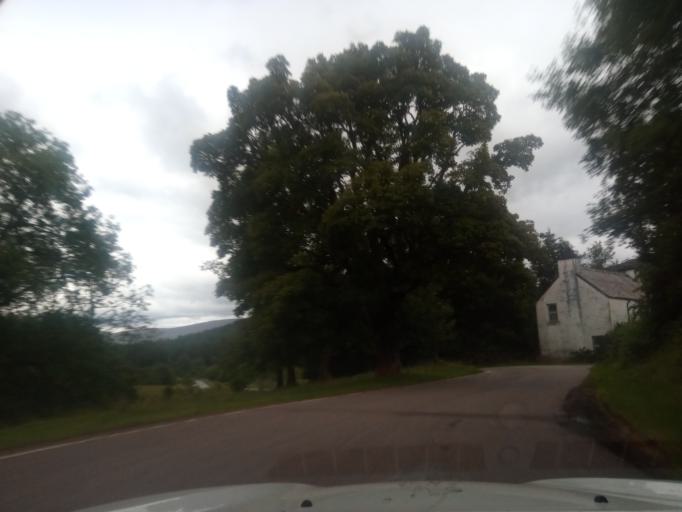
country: GB
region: Scotland
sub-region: Highland
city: Fort William
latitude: 56.8573
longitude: -5.3496
